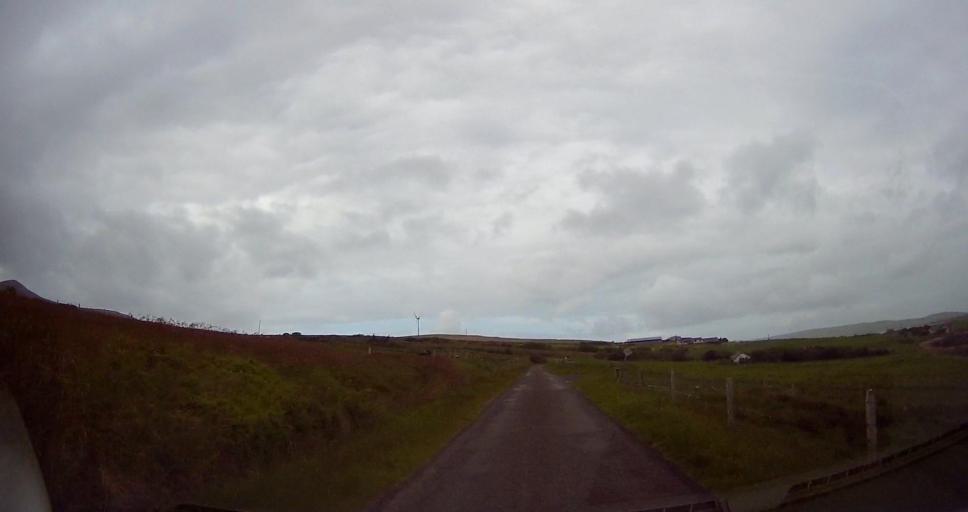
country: GB
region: Scotland
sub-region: Orkney Islands
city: Stromness
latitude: 58.9076
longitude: -3.3185
